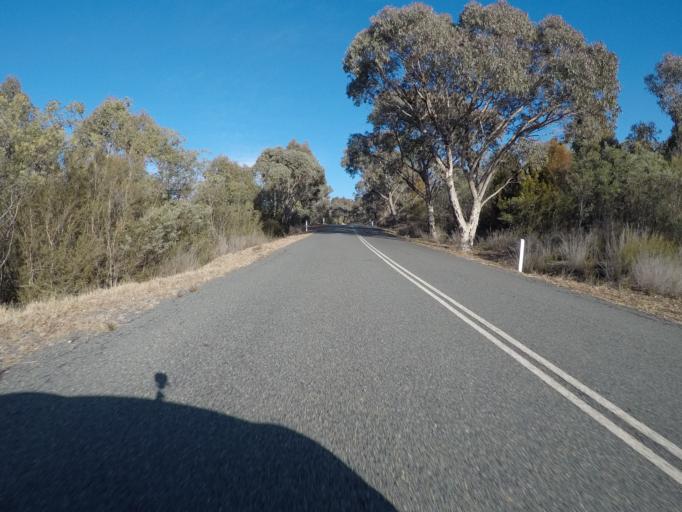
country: AU
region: Australian Capital Territory
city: Macarthur
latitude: -35.4646
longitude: 148.9666
